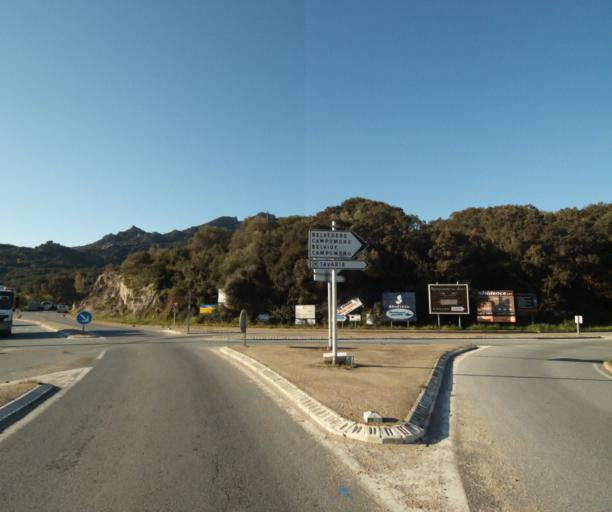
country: FR
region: Corsica
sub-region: Departement de la Corse-du-Sud
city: Propriano
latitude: 41.6567
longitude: 8.9175
